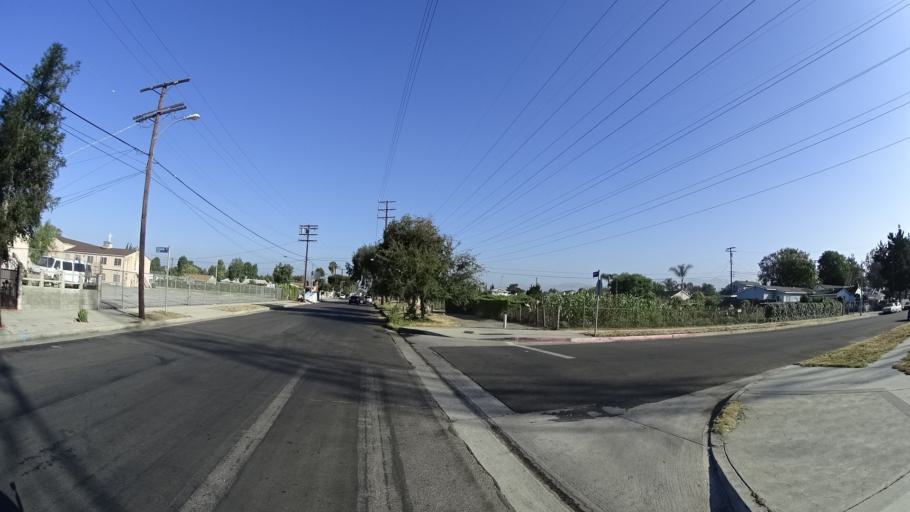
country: US
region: California
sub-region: Los Angeles County
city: Van Nuys
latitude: 34.2306
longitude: -118.4255
